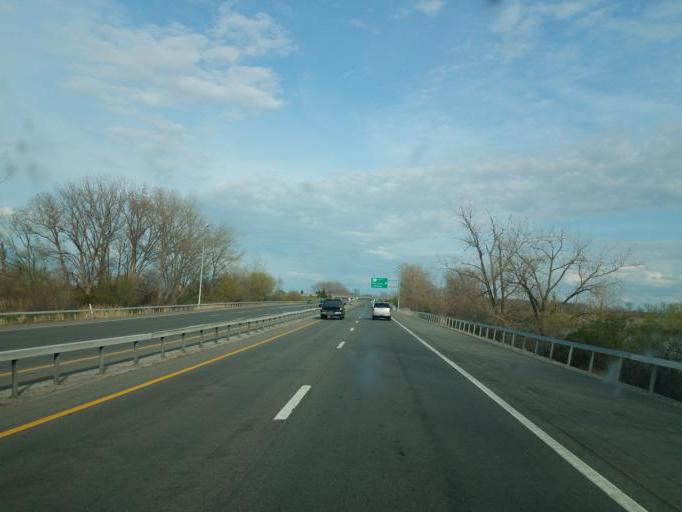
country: US
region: Ohio
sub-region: Erie County
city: Sandusky
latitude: 41.4610
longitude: -82.8255
